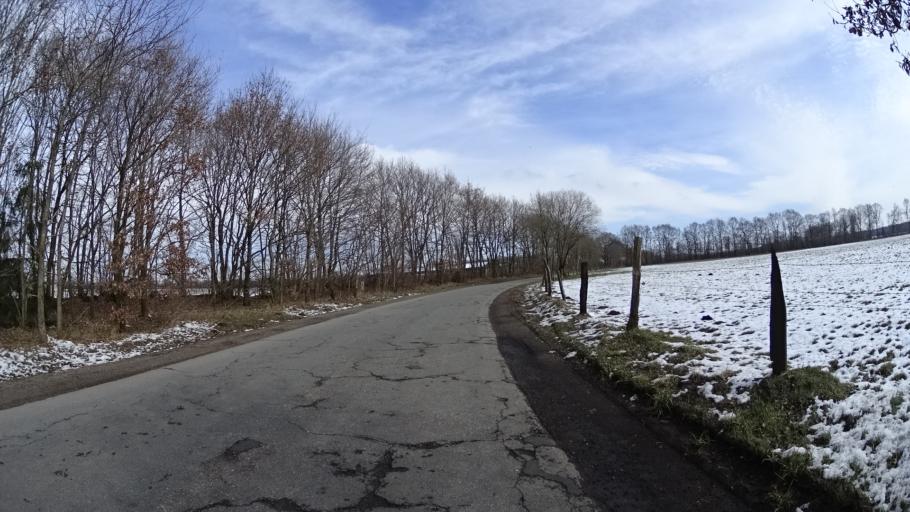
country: DE
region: Schleswig-Holstein
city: Gross Kummerfeld
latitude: 54.0339
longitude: 10.1156
